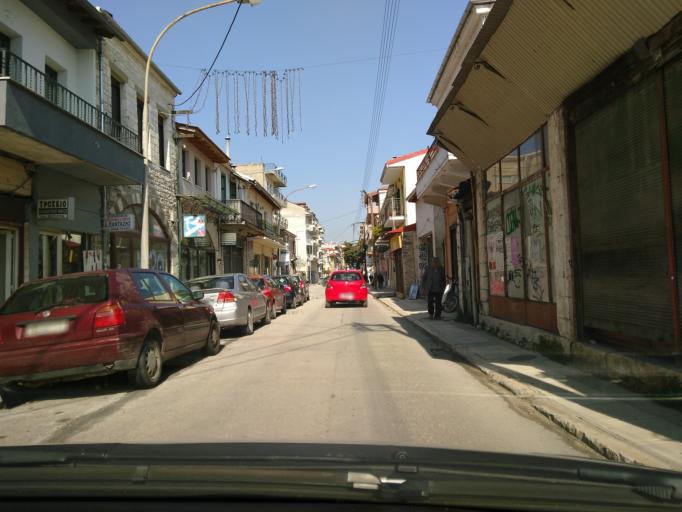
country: GR
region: Epirus
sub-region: Nomos Ioanninon
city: Ioannina
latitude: 39.6711
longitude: 20.8493
